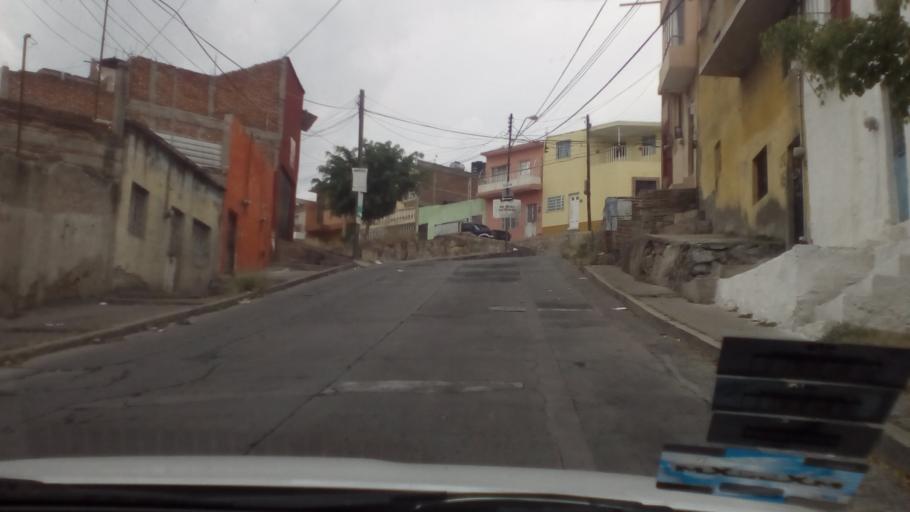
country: MX
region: Guanajuato
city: Leon
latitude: 21.1239
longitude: -101.6885
